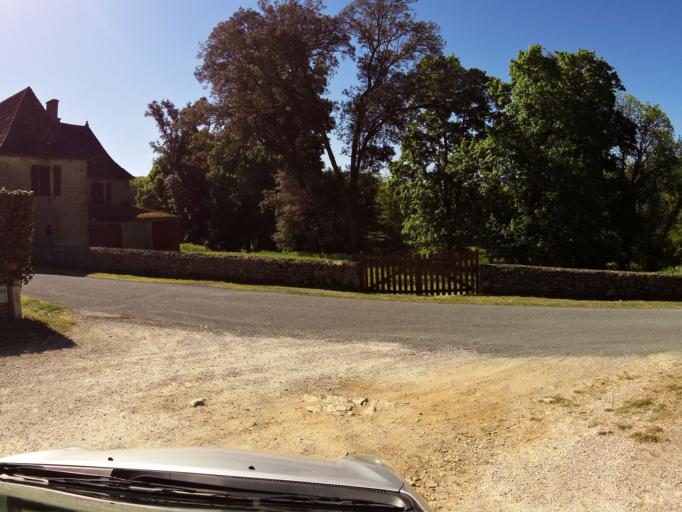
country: FR
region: Aquitaine
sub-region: Departement de la Dordogne
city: Eyvigues-et-Eybenes
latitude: 44.8422
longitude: 1.3469
